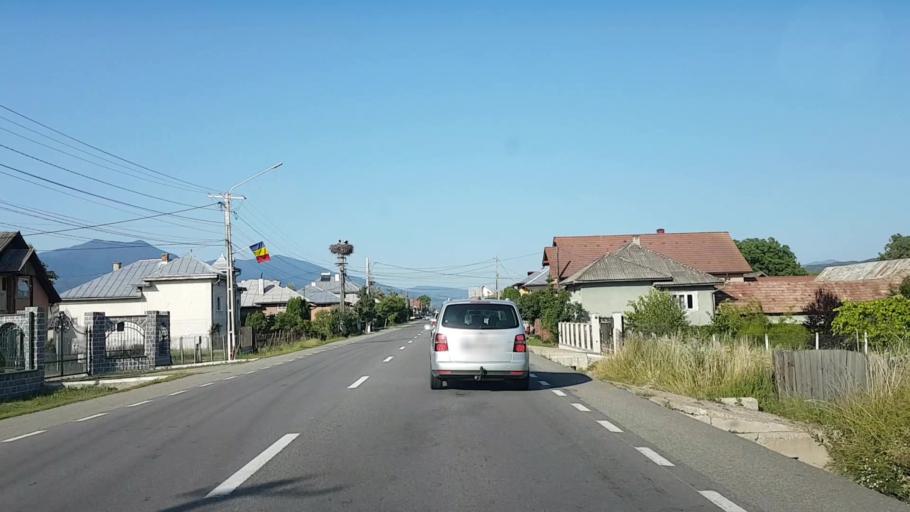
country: RO
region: Bistrita-Nasaud
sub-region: Comuna Josenii Bargaului
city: Josenii Bargaului
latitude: 47.1968
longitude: 24.6300
